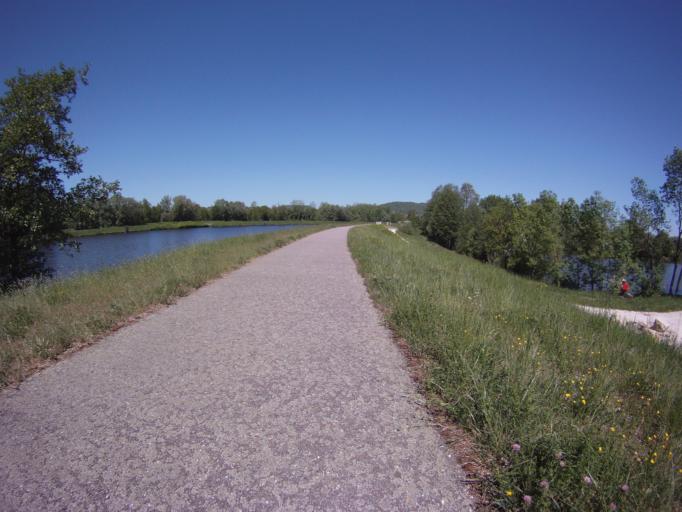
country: FR
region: Lorraine
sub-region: Departement de Meurthe-et-Moselle
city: Dommartin-les-Toul
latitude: 48.6637
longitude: 5.8929
